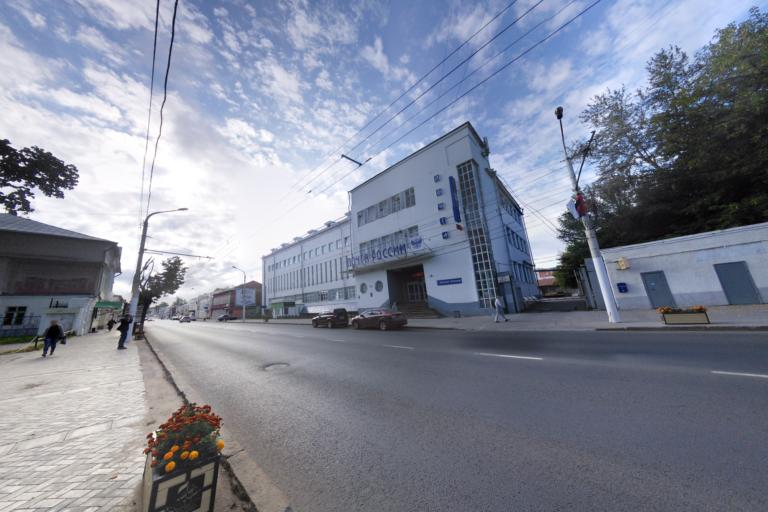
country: RU
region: Kostroma
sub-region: Kostromskoy Rayon
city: Kostroma
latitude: 57.7652
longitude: 40.9334
